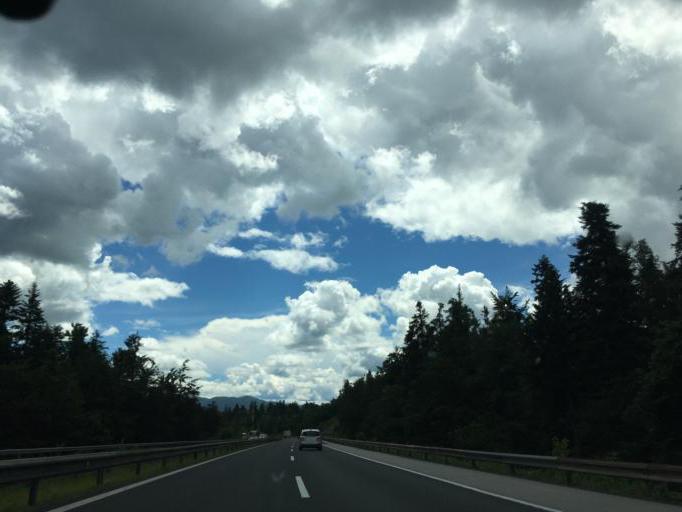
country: SI
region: Logatec
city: Logatec
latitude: 45.8808
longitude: 14.2627
